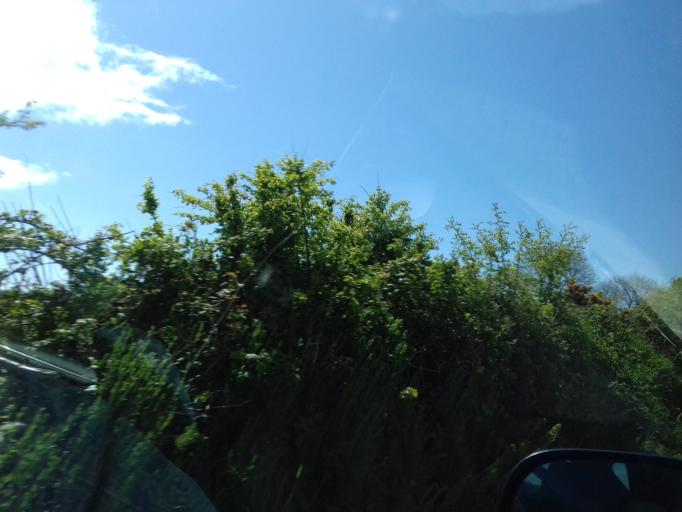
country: IE
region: Munster
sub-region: Waterford
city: Dunmore East
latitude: 52.2341
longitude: -6.8587
